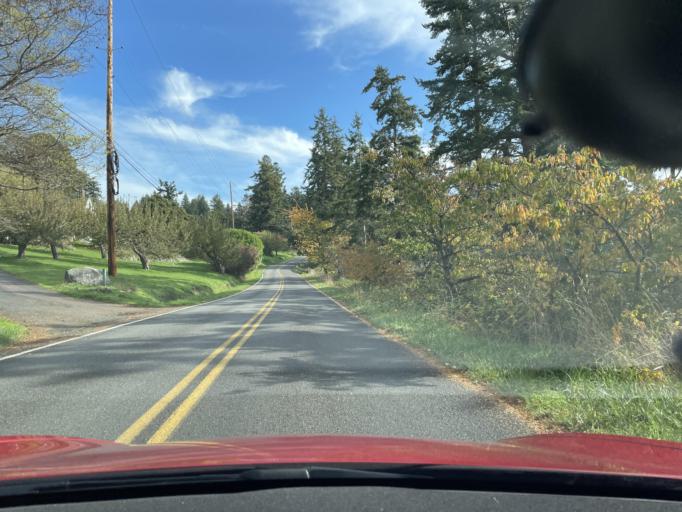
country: US
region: Washington
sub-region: San Juan County
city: Friday Harbor
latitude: 48.5201
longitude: -123.0010
